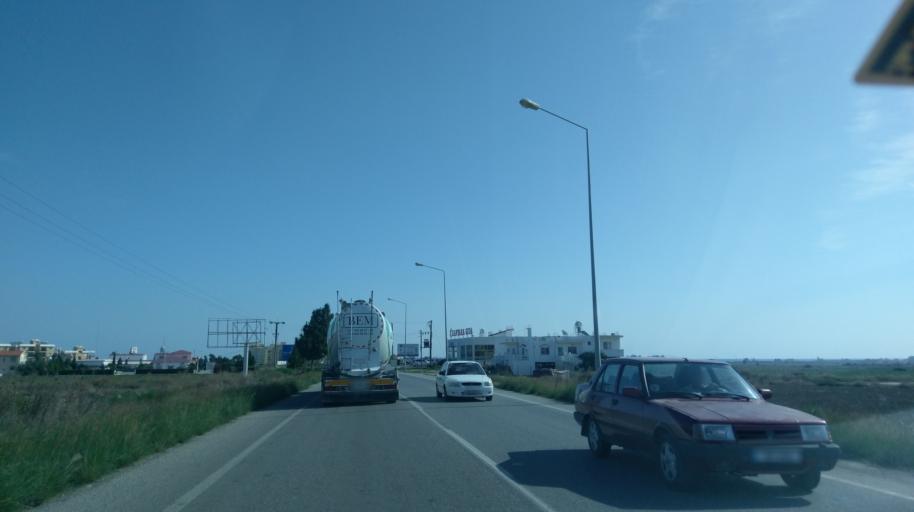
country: CY
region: Ammochostos
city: Trikomo
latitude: 35.2786
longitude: 33.8923
